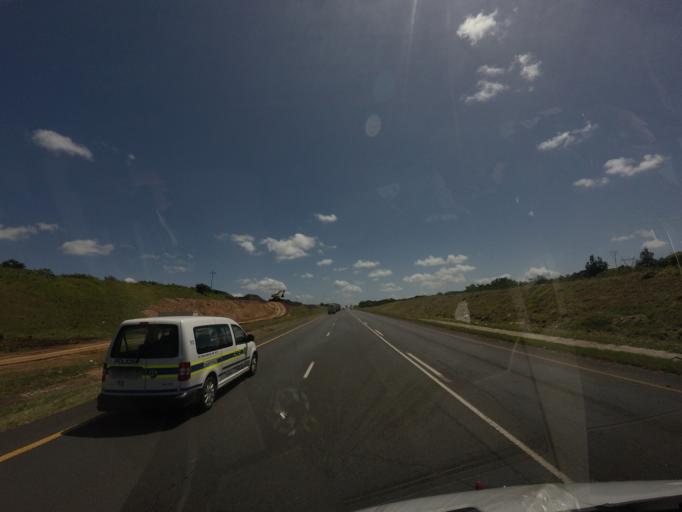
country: ZA
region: KwaZulu-Natal
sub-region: uThungulu District Municipality
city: Empangeni
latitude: -28.7795
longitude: 31.9272
